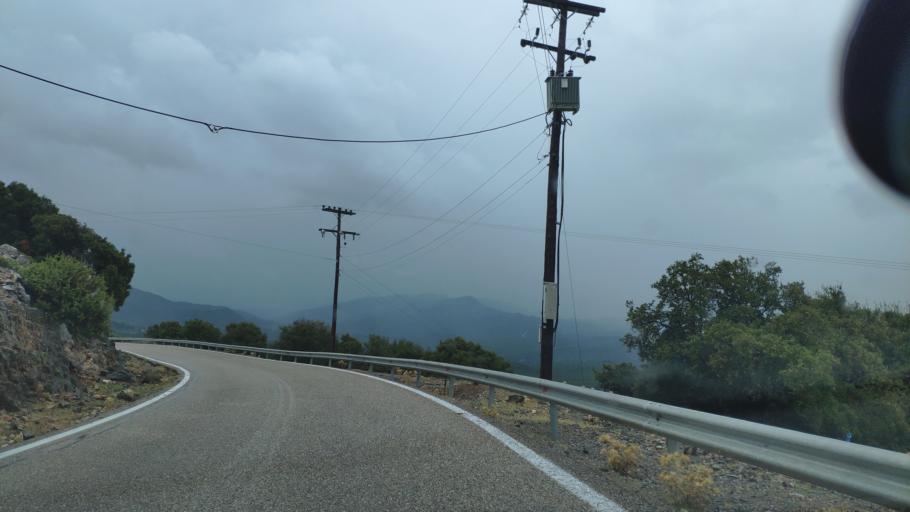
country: GR
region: Central Greece
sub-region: Nomos Evrytanias
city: Kerasochori
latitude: 39.0803
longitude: 21.4061
